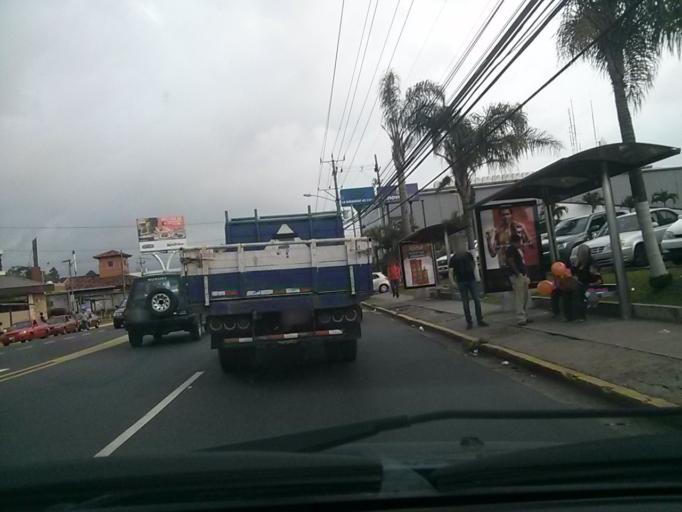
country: CR
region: San Jose
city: San Pedro
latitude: 9.9283
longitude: -84.0422
